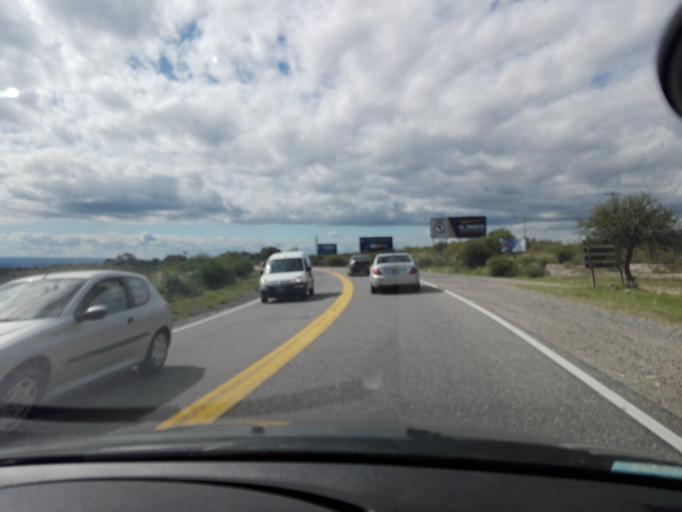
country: AR
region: Cordoba
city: Mina Clavero
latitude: -31.7443
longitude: -64.9342
